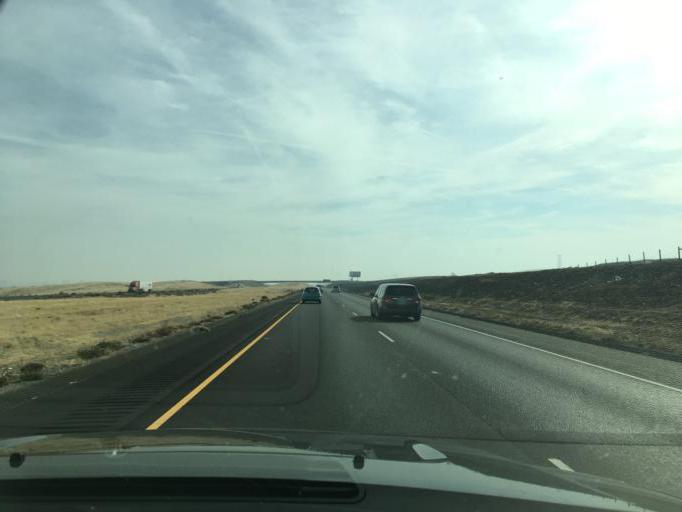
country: US
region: California
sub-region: Kings County
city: Kettleman City
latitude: 36.0132
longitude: -119.9960
